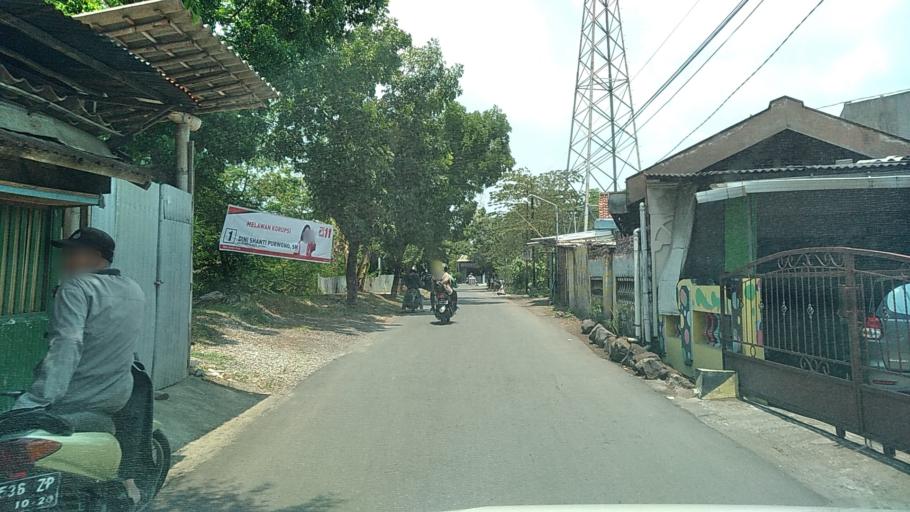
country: ID
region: Central Java
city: Semarang
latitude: -7.0025
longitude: 110.4411
